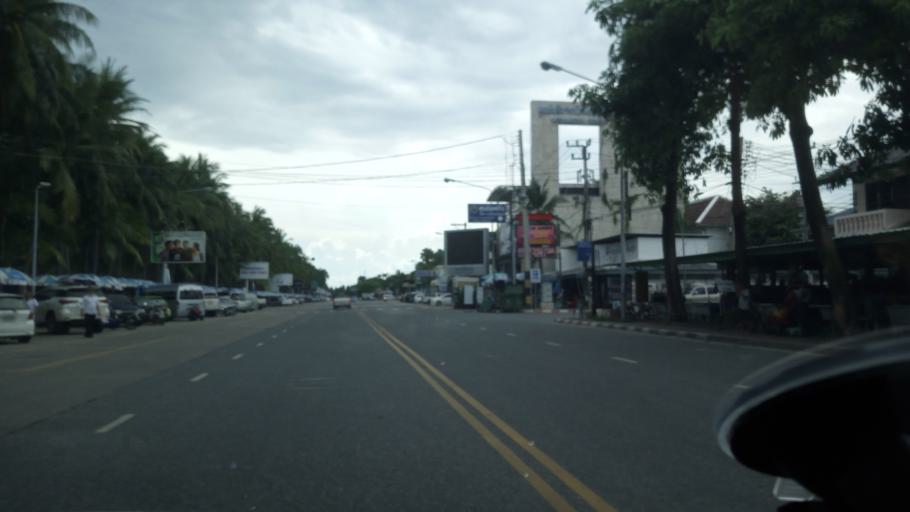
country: TH
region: Chon Buri
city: Chon Buri
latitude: 13.2875
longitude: 100.9126
